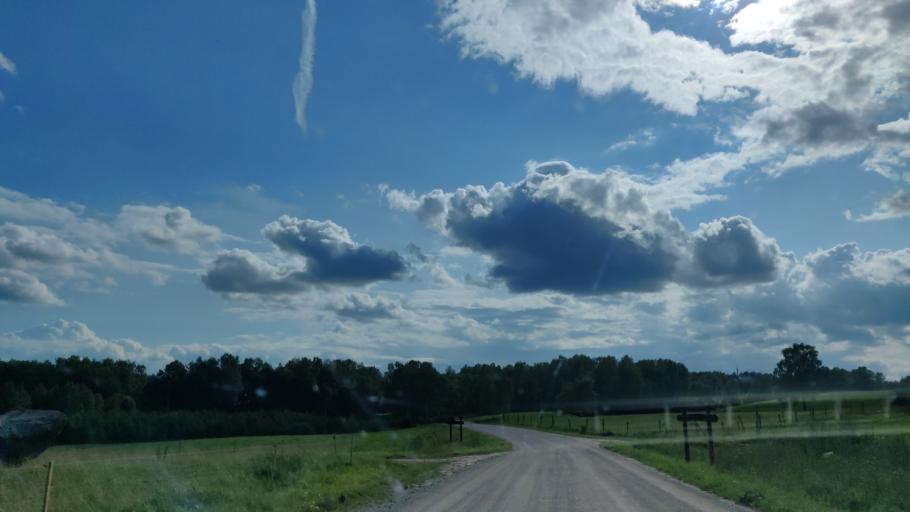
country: LT
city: Varniai
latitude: 55.6039
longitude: 22.3207
